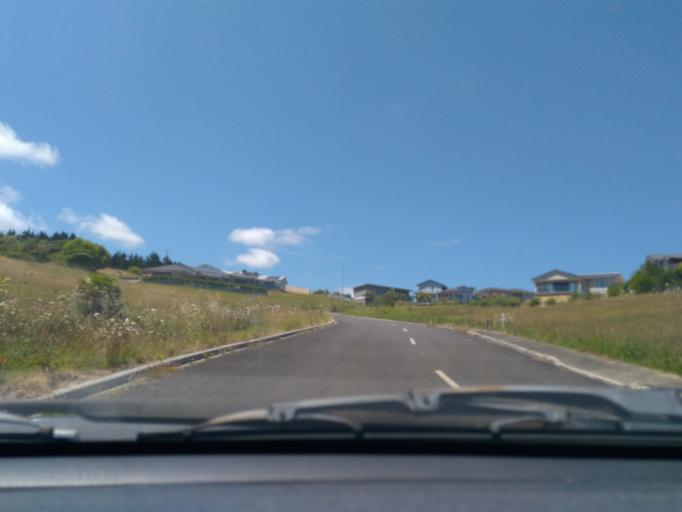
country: NZ
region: Northland
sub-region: Far North District
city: Taipa
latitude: -34.9946
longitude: 173.5090
